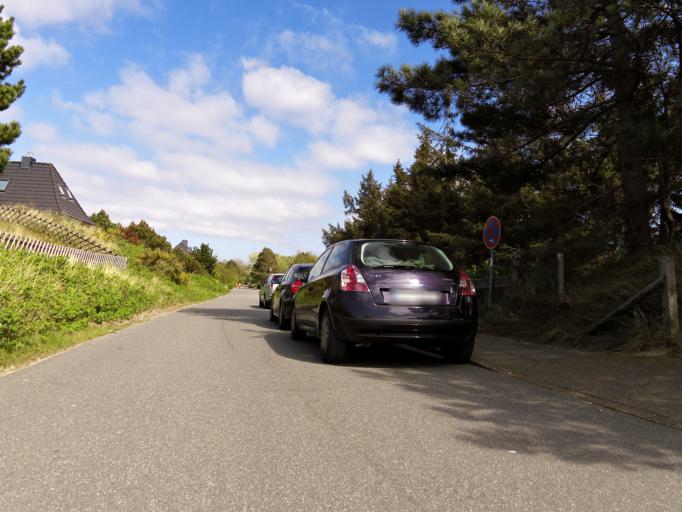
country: DE
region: Schleswig-Holstein
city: Wittdun
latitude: 54.6255
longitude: 8.3842
